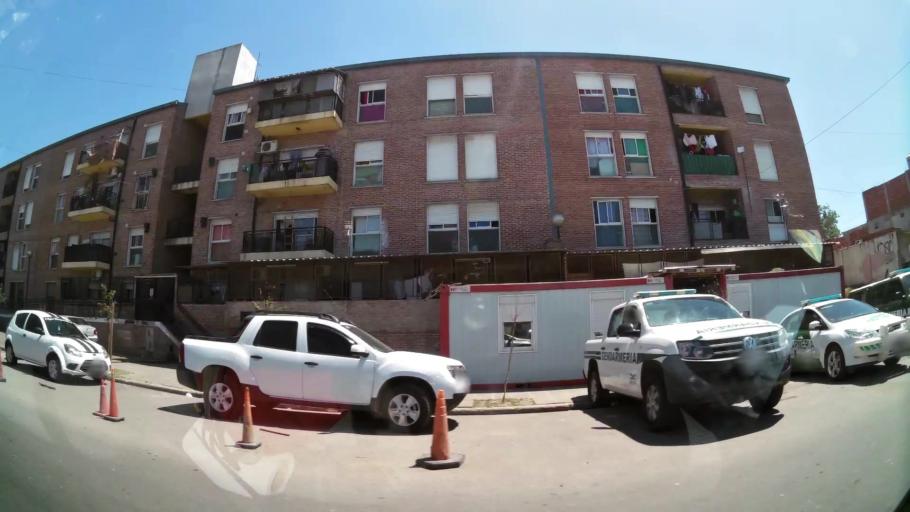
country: AR
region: Buenos Aires
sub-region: Partido de Avellaneda
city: Avellaneda
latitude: -34.6504
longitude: -58.4007
